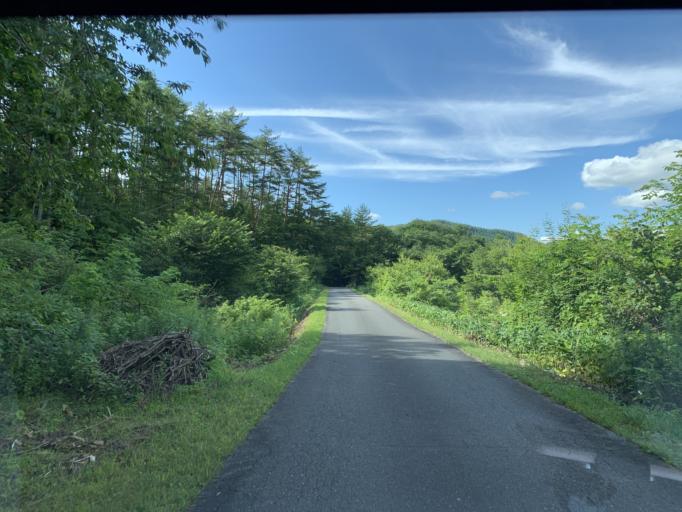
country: JP
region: Iwate
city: Ichinoseki
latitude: 38.9253
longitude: 140.9561
